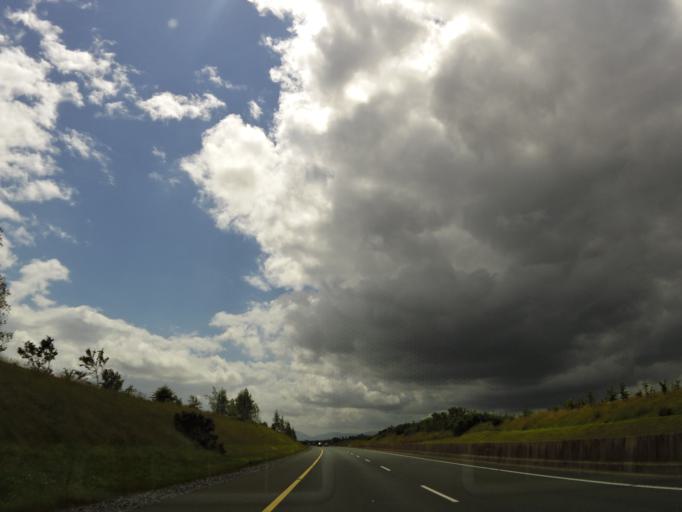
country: IE
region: Munster
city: Cashel
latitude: 52.4794
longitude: -7.9063
